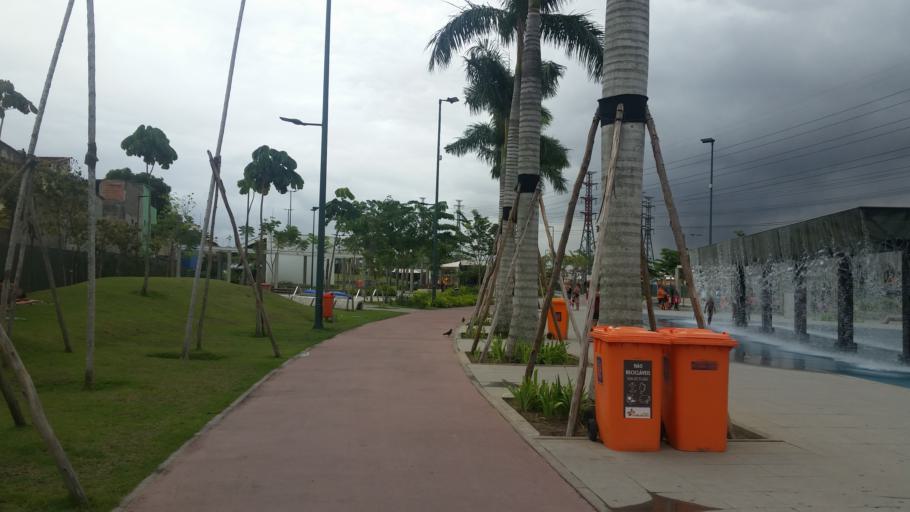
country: BR
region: Rio de Janeiro
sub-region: Sao Joao De Meriti
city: Sao Joao de Meriti
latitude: -22.8587
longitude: -43.3499
